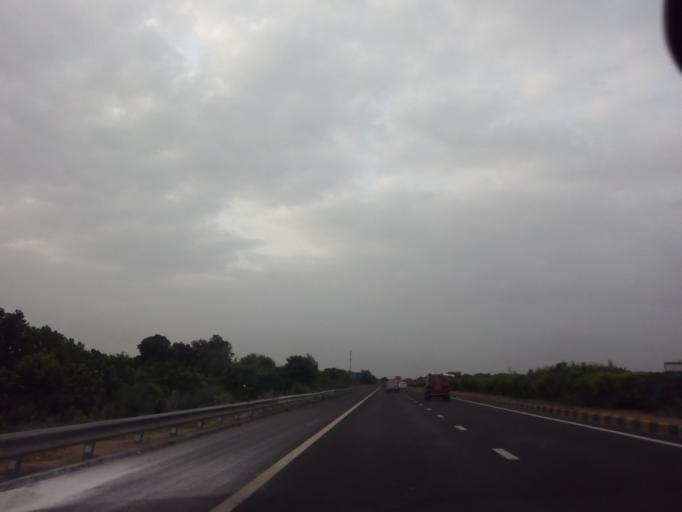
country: IN
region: Gujarat
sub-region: Kheda
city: Mahemdavad
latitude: 22.8997
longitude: 72.7767
